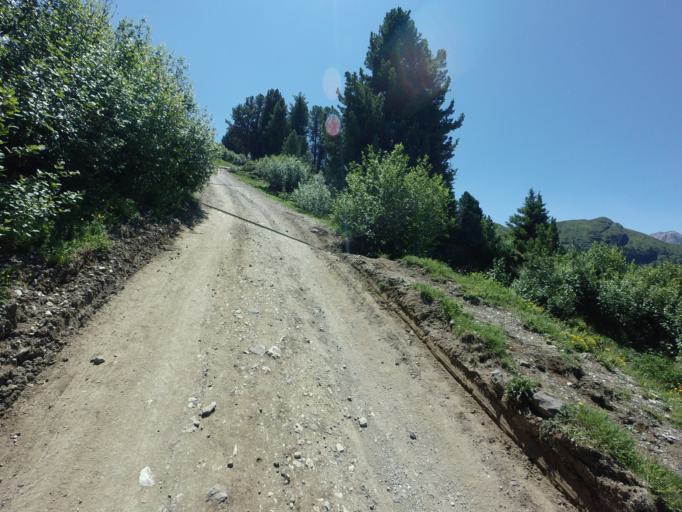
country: IT
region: Trentino-Alto Adige
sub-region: Provincia di Trento
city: Mazzin
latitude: 46.5111
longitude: 11.6918
